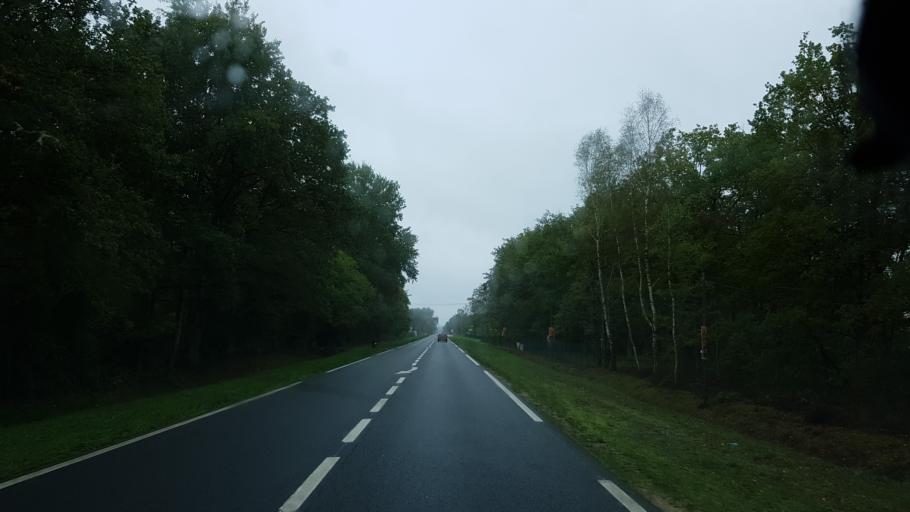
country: FR
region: Centre
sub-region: Departement du Loir-et-Cher
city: Salbris
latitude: 47.4436
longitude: 2.0461
